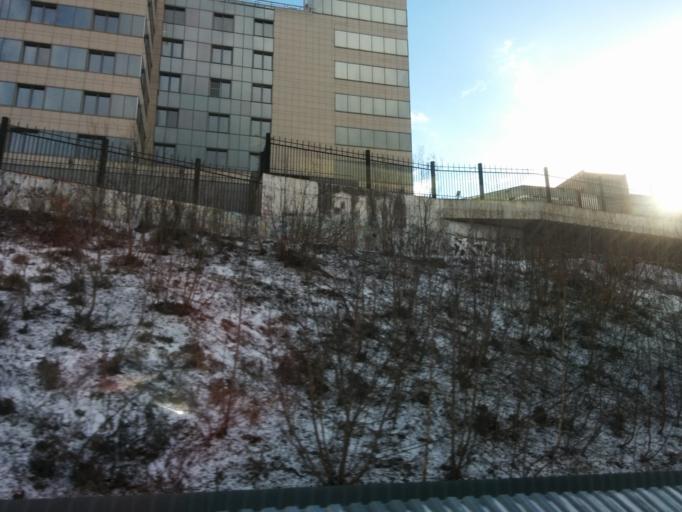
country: RU
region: Moskovskaya
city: Presnenskiy
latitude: 55.7433
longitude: 37.5291
